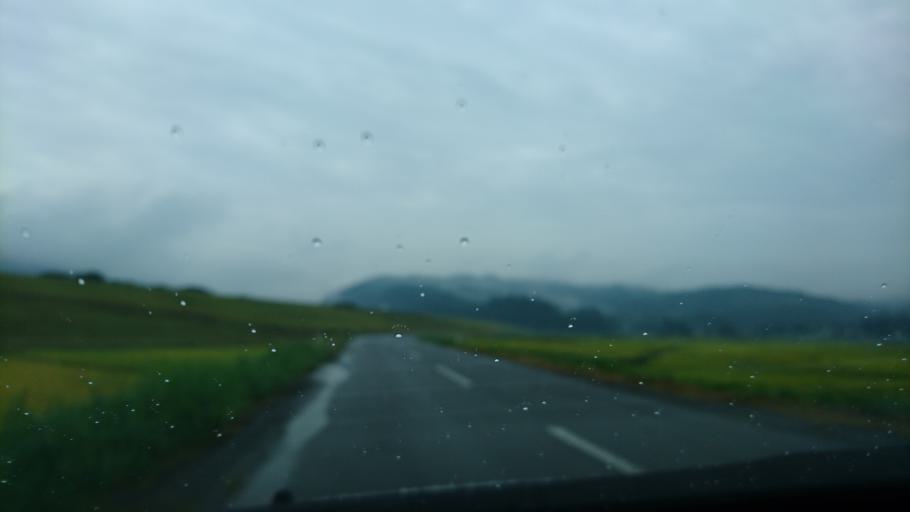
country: JP
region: Iwate
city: Ichinoseki
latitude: 38.8860
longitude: 141.2594
